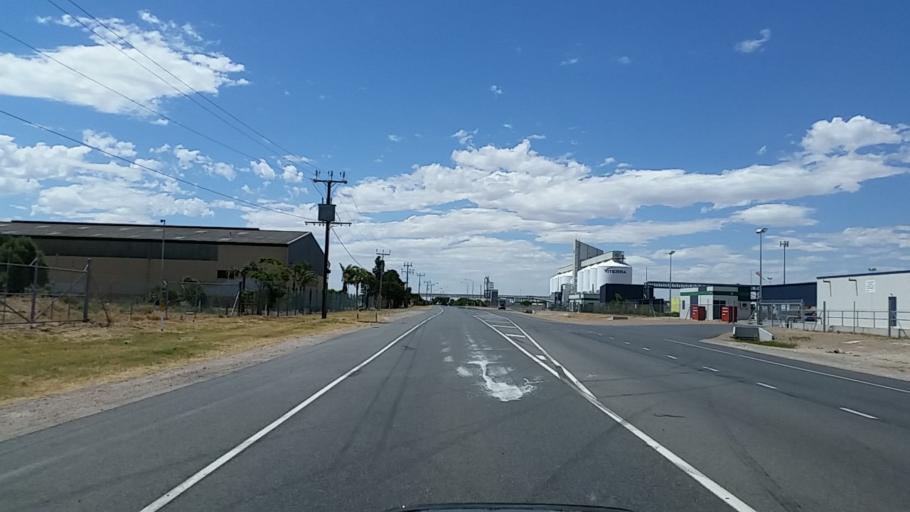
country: AU
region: South Australia
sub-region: Port Adelaide Enfield
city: Birkenhead
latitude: -34.7764
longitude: 138.5016
